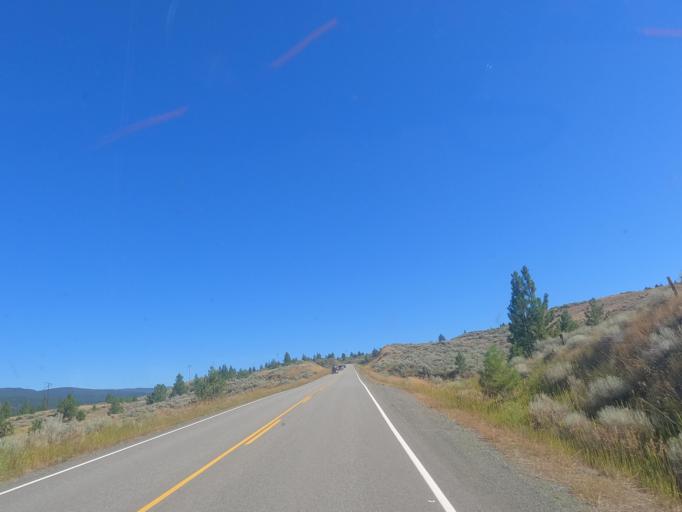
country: CA
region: British Columbia
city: Merritt
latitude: 50.1867
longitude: -120.8529
